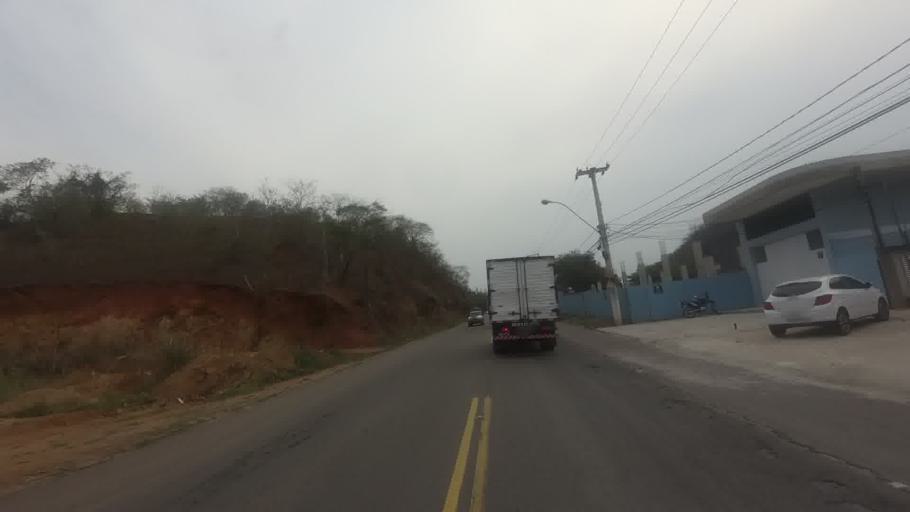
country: BR
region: Rio de Janeiro
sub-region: Santo Antonio De Padua
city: Santo Antonio de Padua
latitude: -21.5577
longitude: -42.1810
